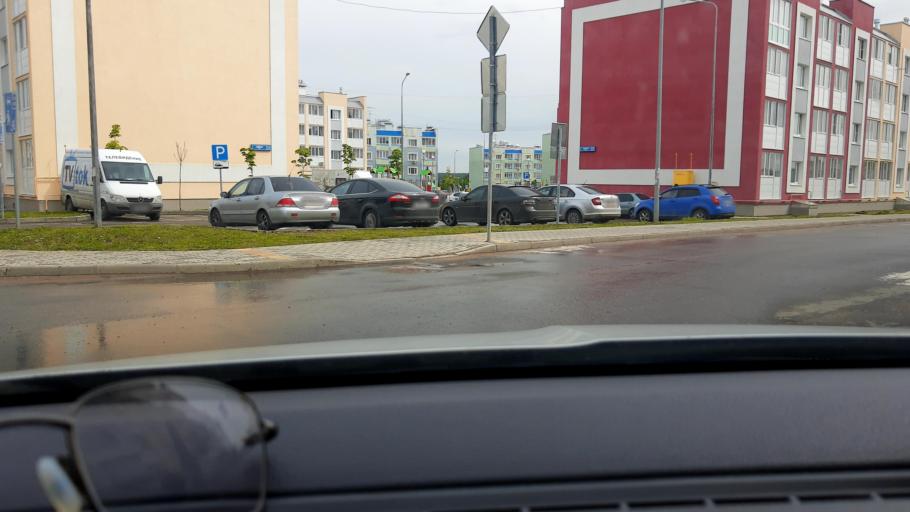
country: RU
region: Moskovskaya
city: Dedovsk
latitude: 55.8392
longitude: 37.1254
